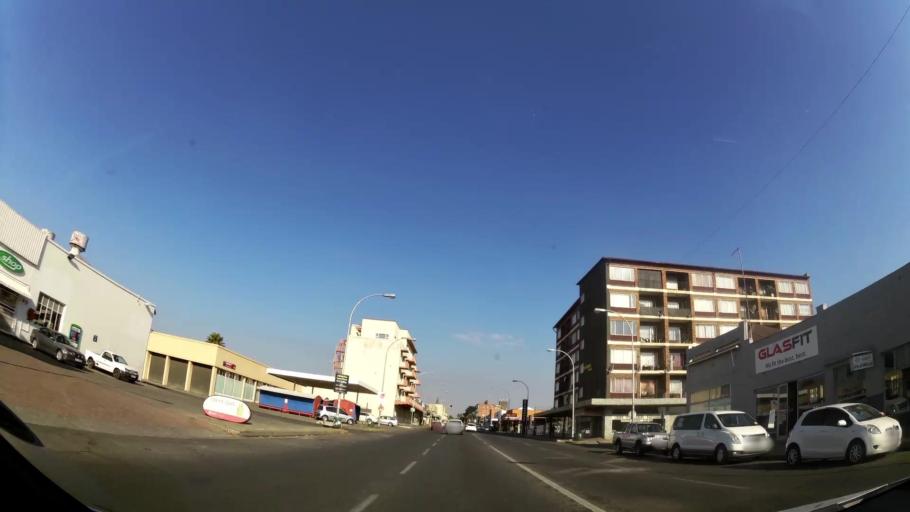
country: ZA
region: Gauteng
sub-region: Ekurhuleni Metropolitan Municipality
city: Brakpan
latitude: -26.2422
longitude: 28.3674
